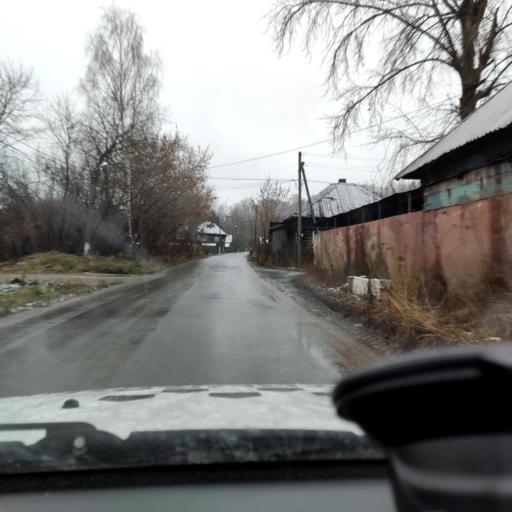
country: RU
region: Perm
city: Perm
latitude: 58.0583
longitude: 56.3308
